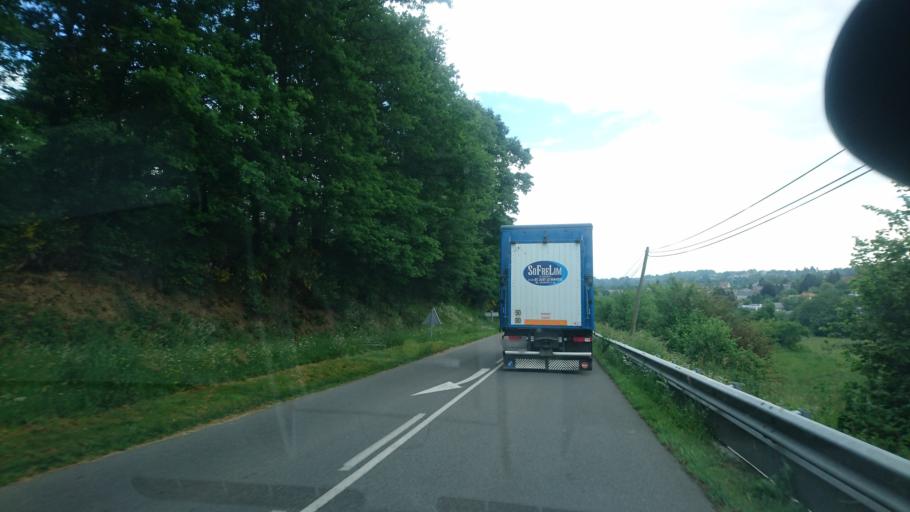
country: FR
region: Limousin
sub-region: Departement de la Haute-Vienne
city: Chateauneuf-la-Foret
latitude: 45.7063
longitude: 1.5953
